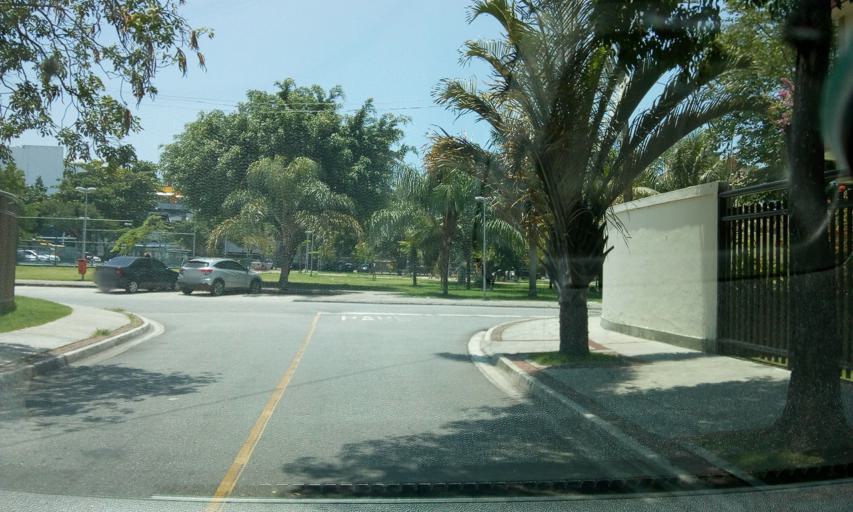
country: BR
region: Rio de Janeiro
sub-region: Nilopolis
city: Nilopolis
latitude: -23.0194
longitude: -43.4615
